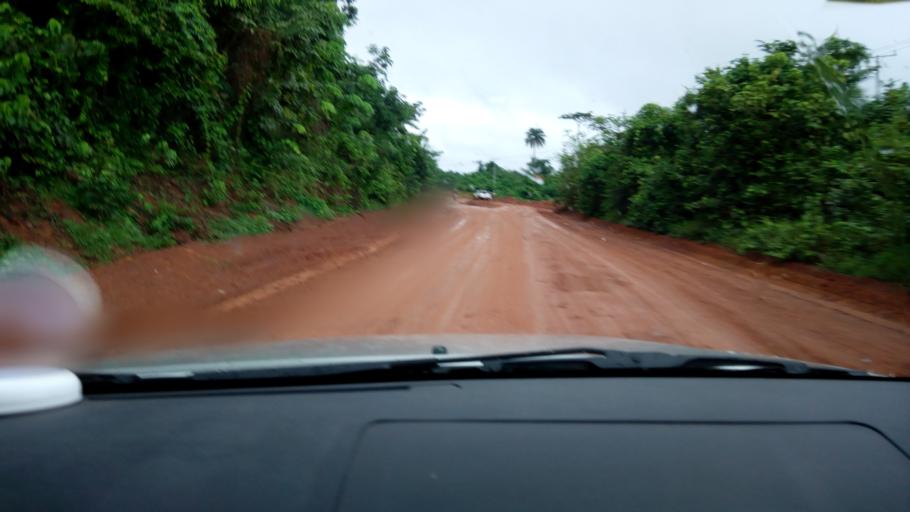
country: LR
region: Nimba
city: Sanniquellie
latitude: 7.1820
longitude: -8.9687
